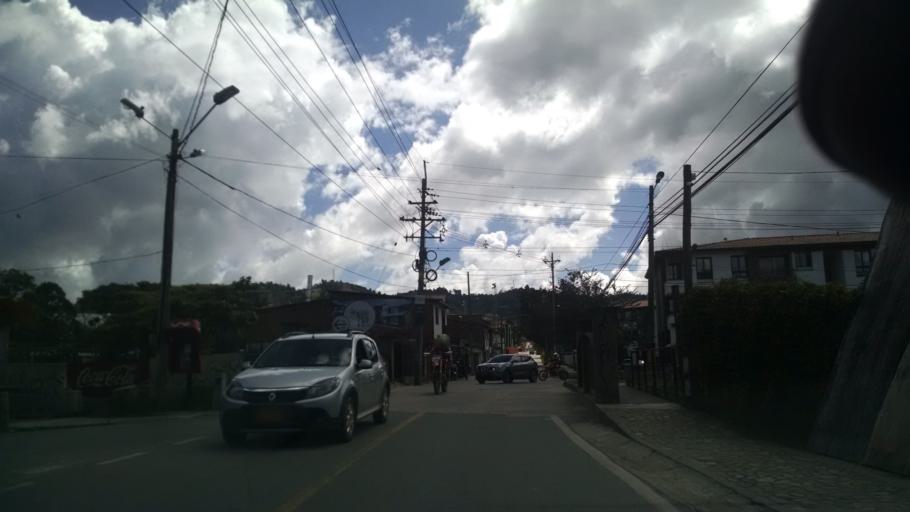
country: CO
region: Antioquia
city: El Retiro
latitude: 6.0647
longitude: -75.5010
